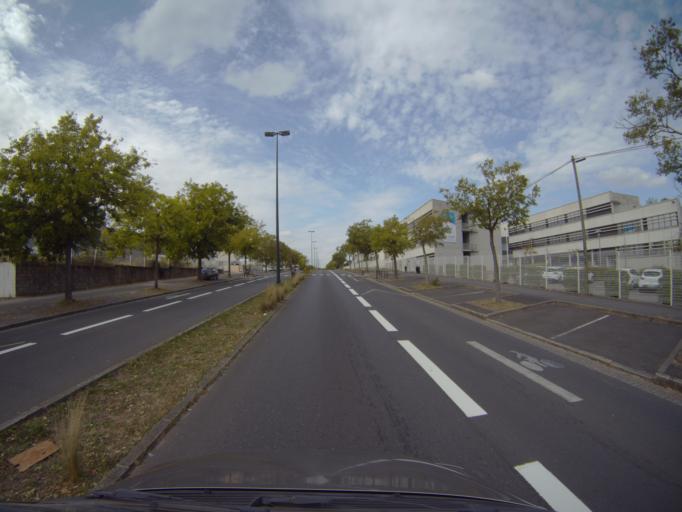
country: FR
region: Pays de la Loire
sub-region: Departement de la Loire-Atlantique
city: Bouguenais
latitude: 47.1985
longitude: -1.6071
